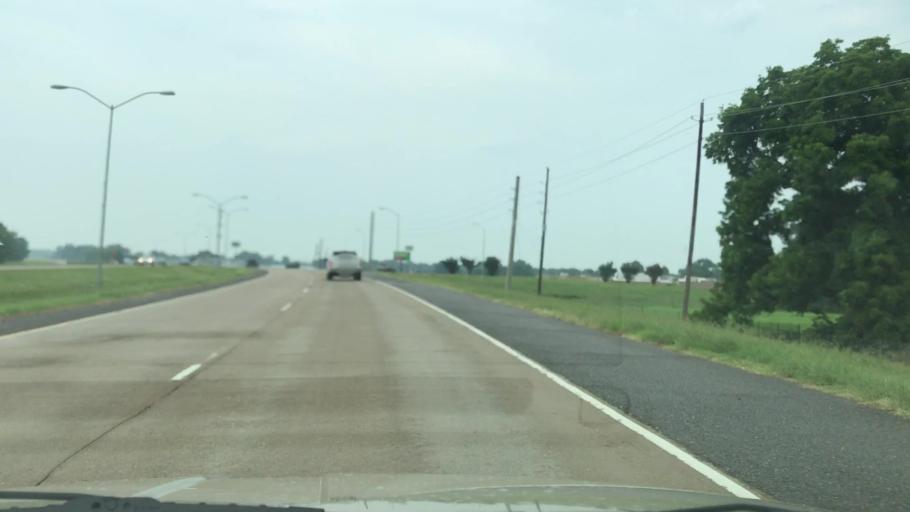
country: US
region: Louisiana
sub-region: Bossier Parish
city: Bossier City
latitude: 32.4765
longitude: -93.6792
